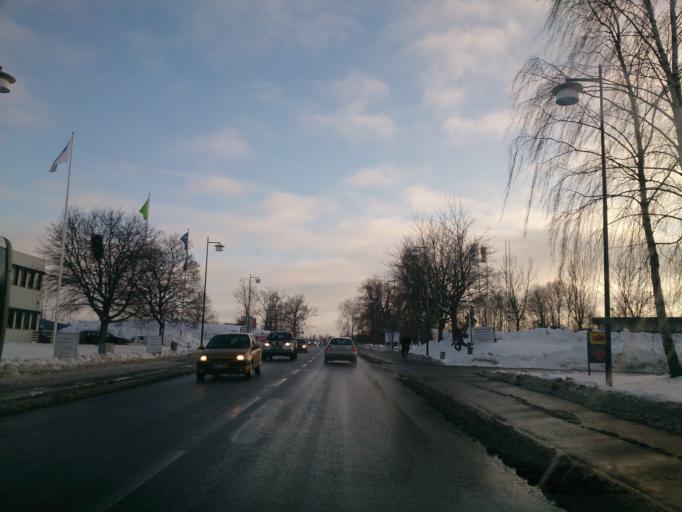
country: SE
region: OEstergoetland
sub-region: Norrkopings Kommun
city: Norrkoping
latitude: 58.6164
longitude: 16.1556
